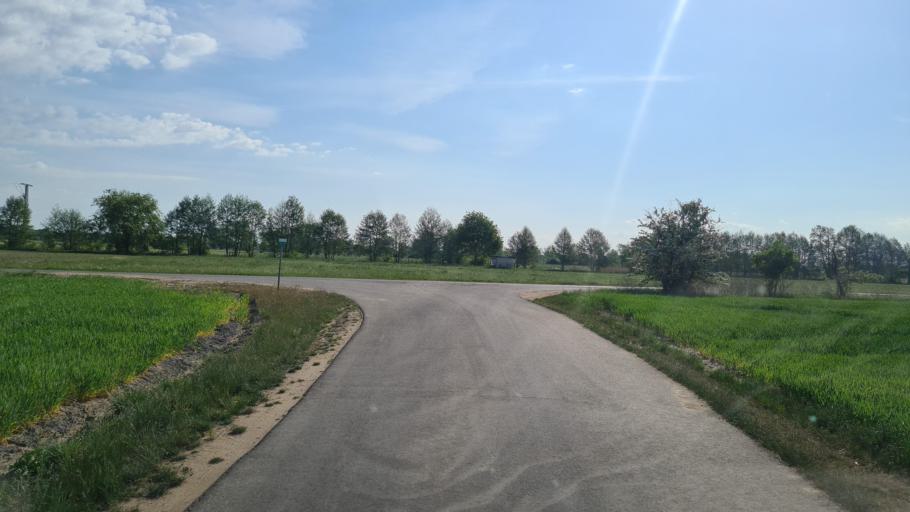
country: DE
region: Brandenburg
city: Falkenberg
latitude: 51.5866
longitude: 13.2073
